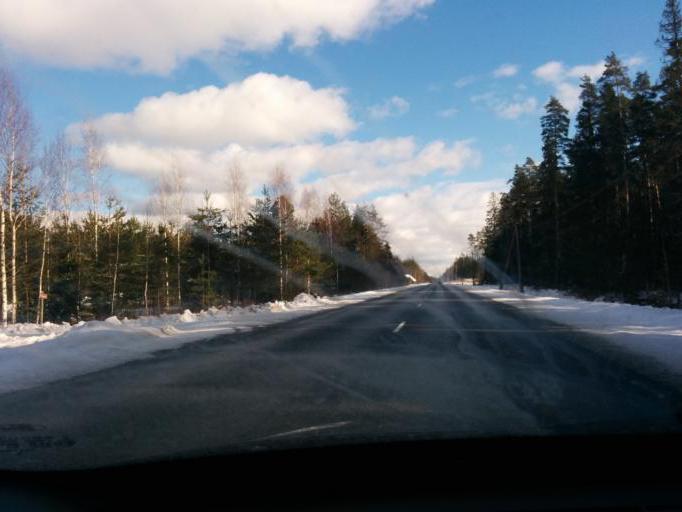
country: LV
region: Jaunpiebalga
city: Jaunpiebalga
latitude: 57.2383
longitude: 26.2368
